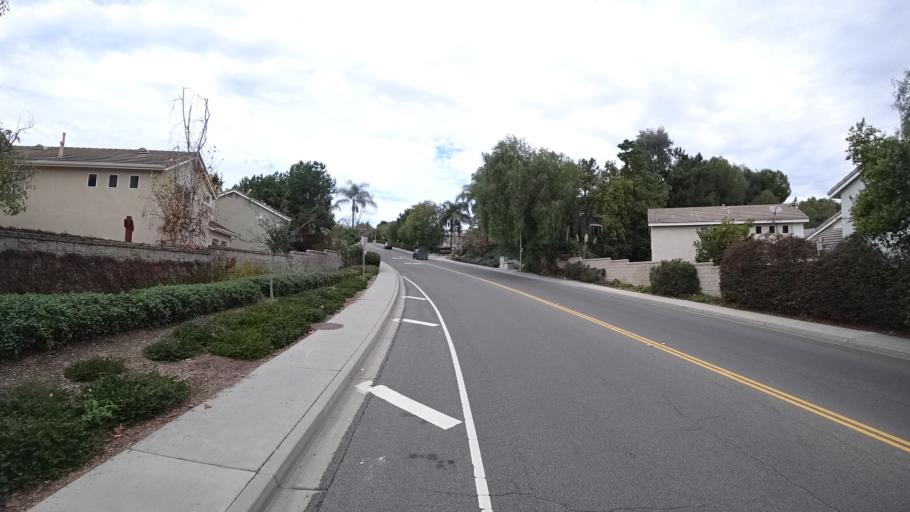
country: US
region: California
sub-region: Orange County
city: Aliso Viejo
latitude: 33.5683
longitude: -117.7334
